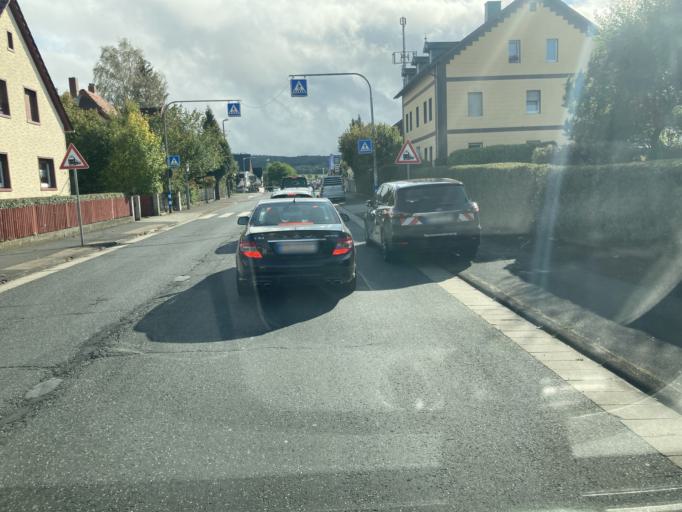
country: DE
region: Hesse
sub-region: Regierungsbezirk Darmstadt
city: Wehrheim
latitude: 50.2972
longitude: 8.5683
